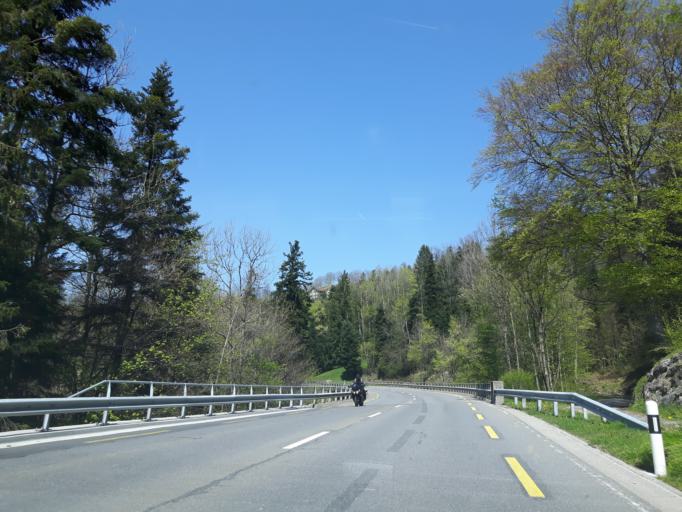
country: CH
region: Schwyz
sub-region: Bezirk Schwyz
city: Steinen
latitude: 47.0438
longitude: 8.6354
